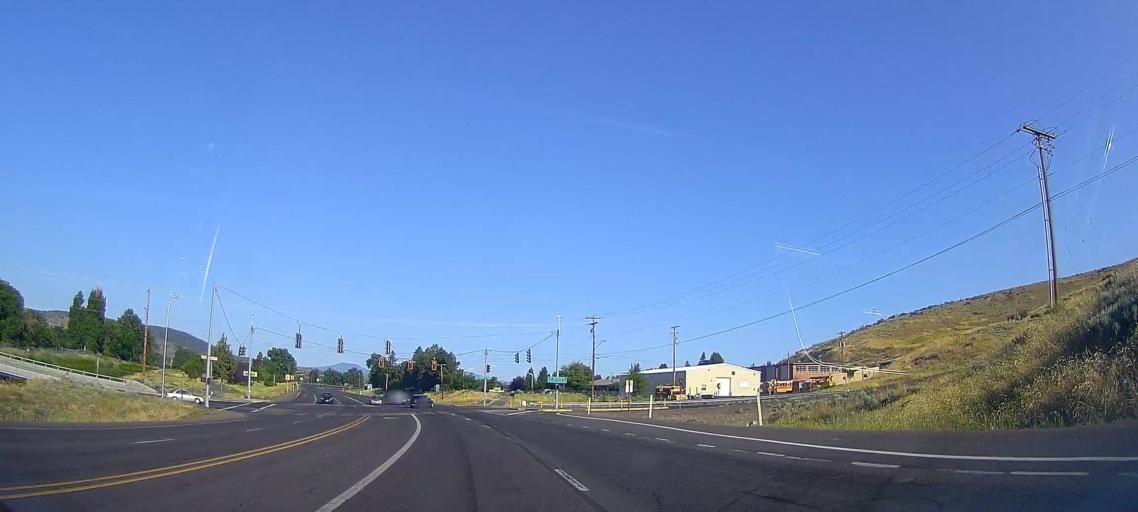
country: US
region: Oregon
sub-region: Klamath County
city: Klamath Falls
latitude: 42.2247
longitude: -121.7563
